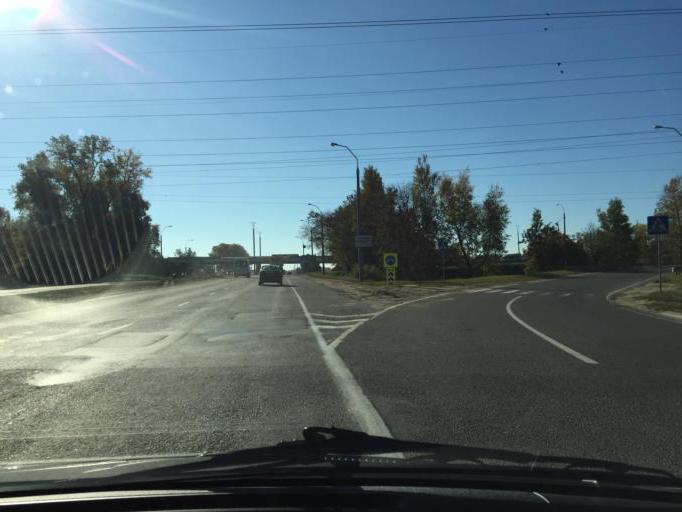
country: BY
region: Minsk
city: Syenitsa
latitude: 53.8378
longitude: 27.5331
